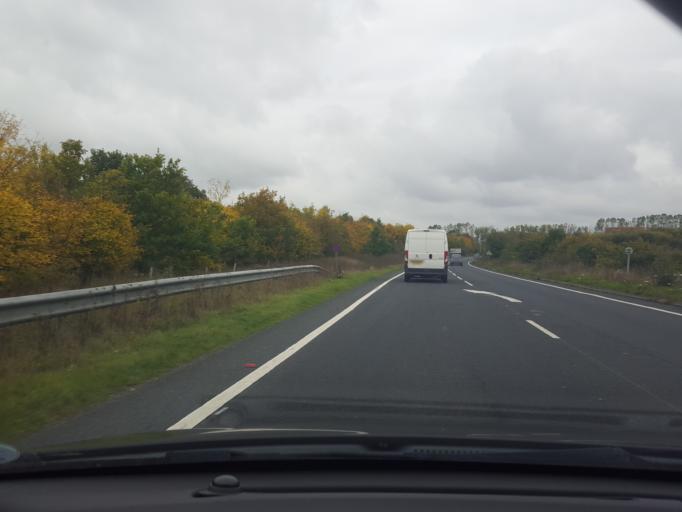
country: GB
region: England
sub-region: Essex
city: Great Bentley
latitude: 51.8561
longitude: 1.1010
